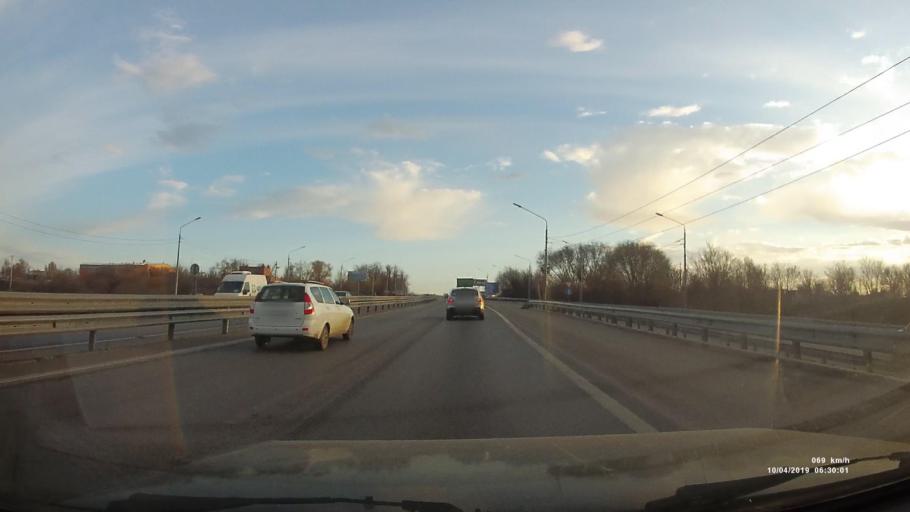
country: RU
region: Rostov
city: Aksay
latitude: 47.2498
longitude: 39.8464
